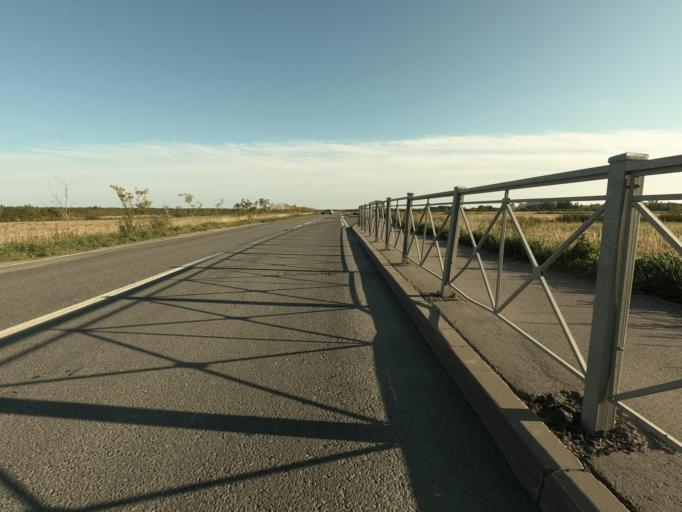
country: RU
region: St.-Petersburg
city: Sapernyy
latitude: 59.7544
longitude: 30.6328
